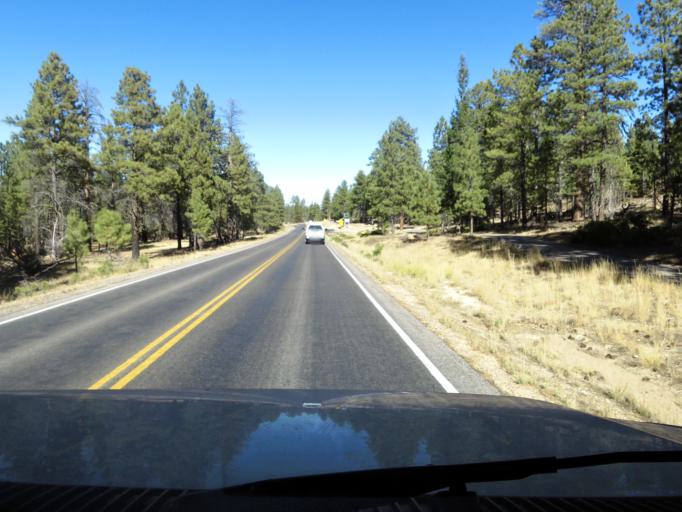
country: US
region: Utah
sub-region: Garfield County
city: Panguitch
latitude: 37.6206
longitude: -112.1733
